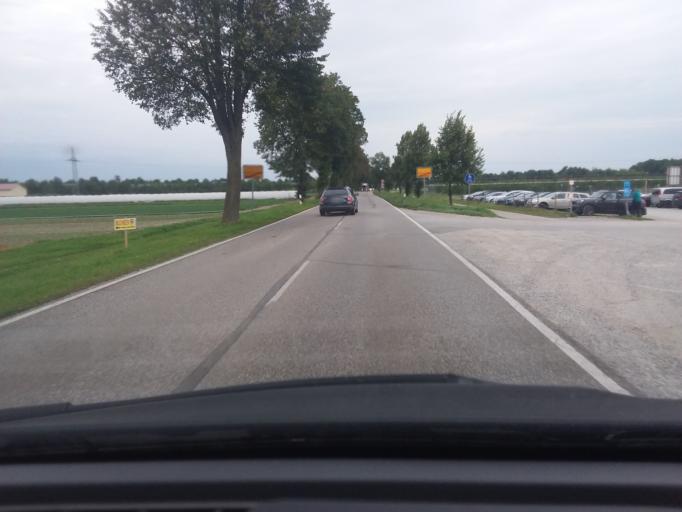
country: DE
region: Bavaria
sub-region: Upper Bavaria
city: Oberschleissheim
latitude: 48.2203
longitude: 11.5313
